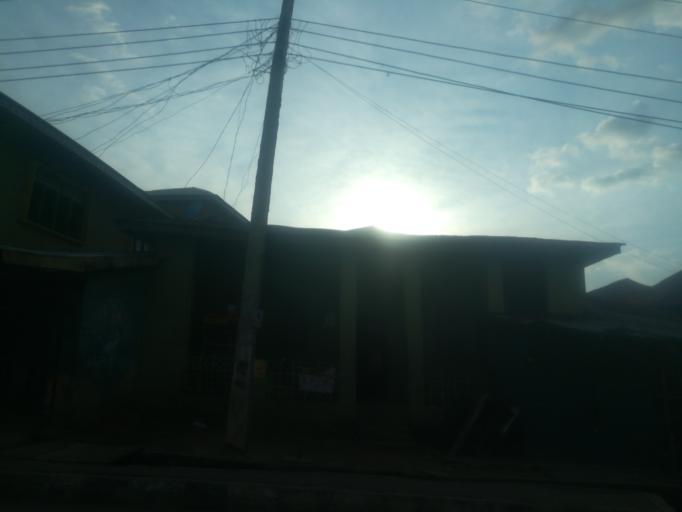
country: NG
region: Oyo
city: Ibadan
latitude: 7.3835
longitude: 3.8815
